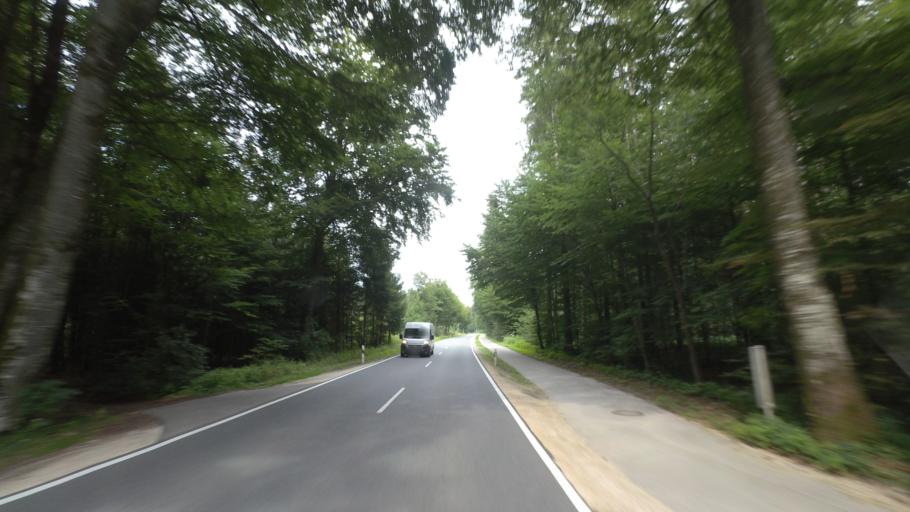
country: DE
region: Bavaria
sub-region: Upper Bavaria
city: Obing
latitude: 47.9851
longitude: 12.4112
